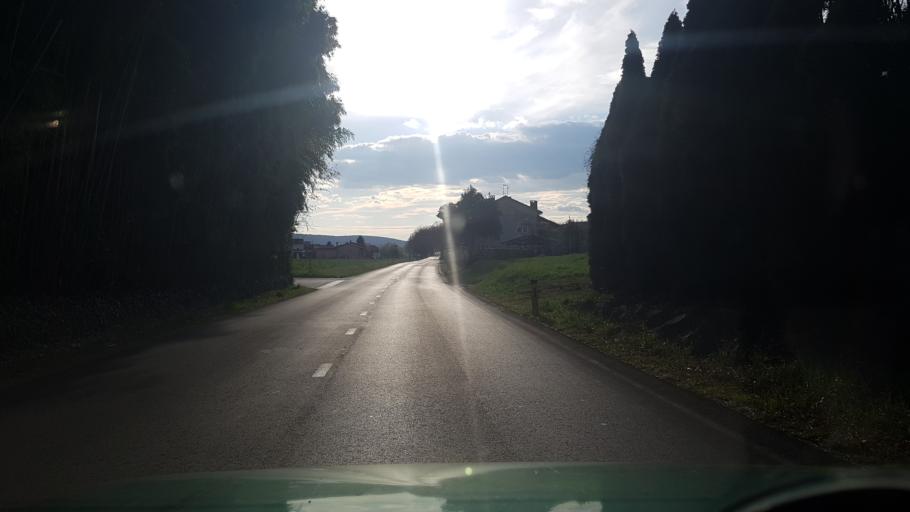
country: SI
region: Rence-Vogrsko
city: Rence
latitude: 45.8981
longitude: 13.6639
